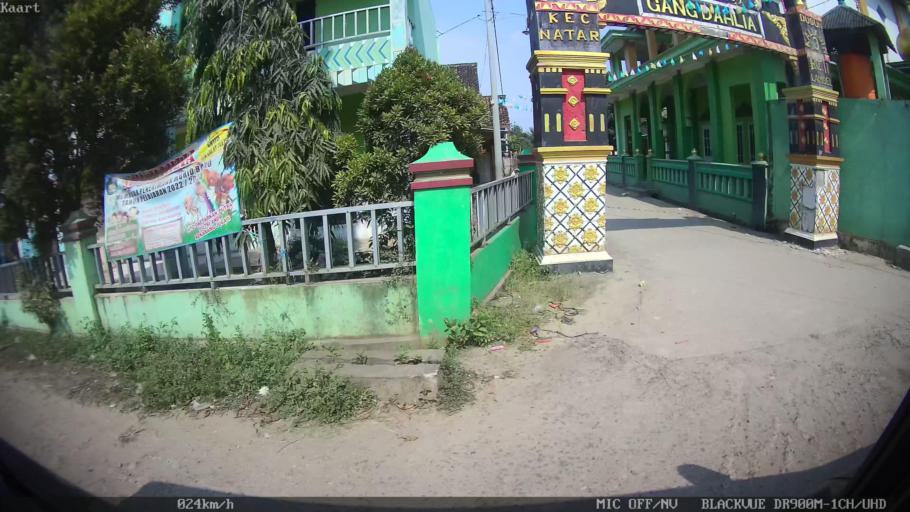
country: ID
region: Lampung
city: Natar
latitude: -5.3005
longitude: 105.2243
